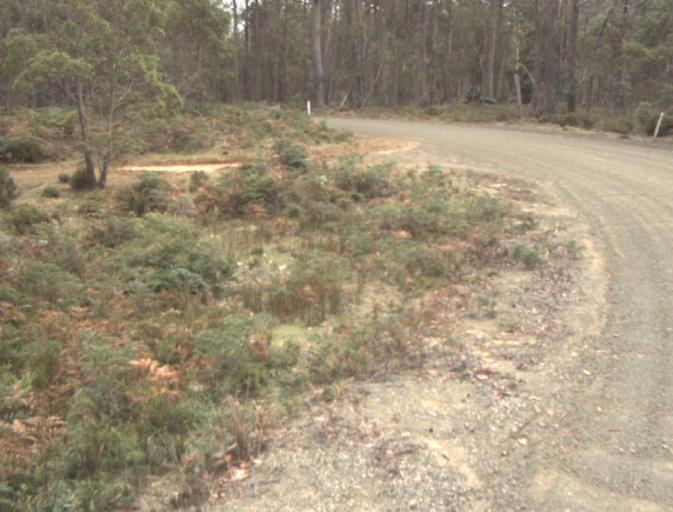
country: AU
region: Tasmania
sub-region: Dorset
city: Scottsdale
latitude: -41.4984
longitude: 147.6034
